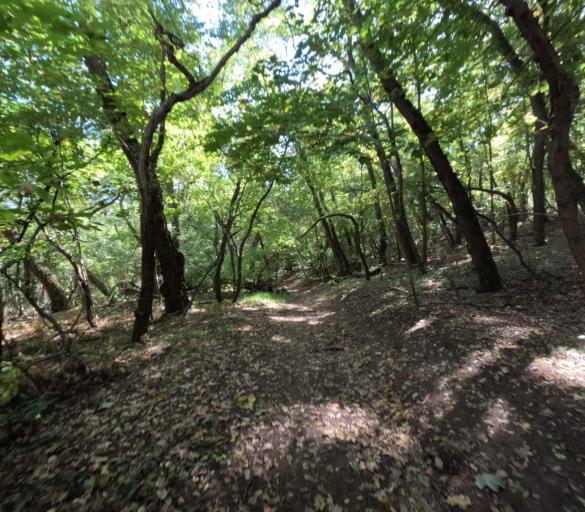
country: DE
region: Saxony
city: Albertstadt
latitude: 51.1074
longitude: 13.7416
